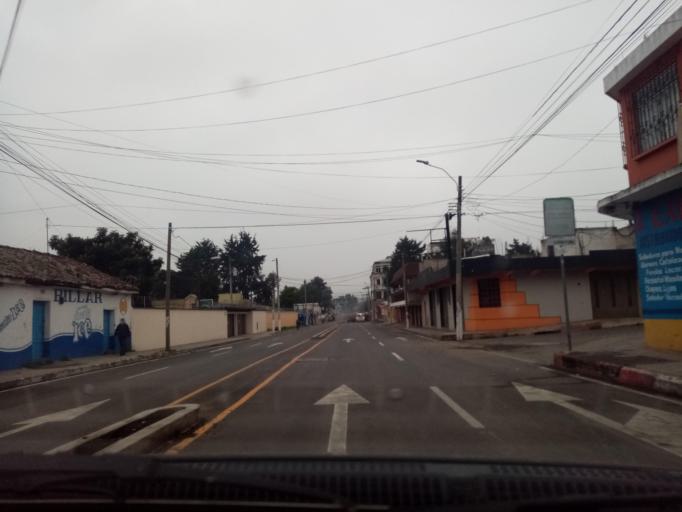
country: GT
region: Quetzaltenango
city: Quetzaltenango
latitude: 14.8458
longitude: -91.5179
